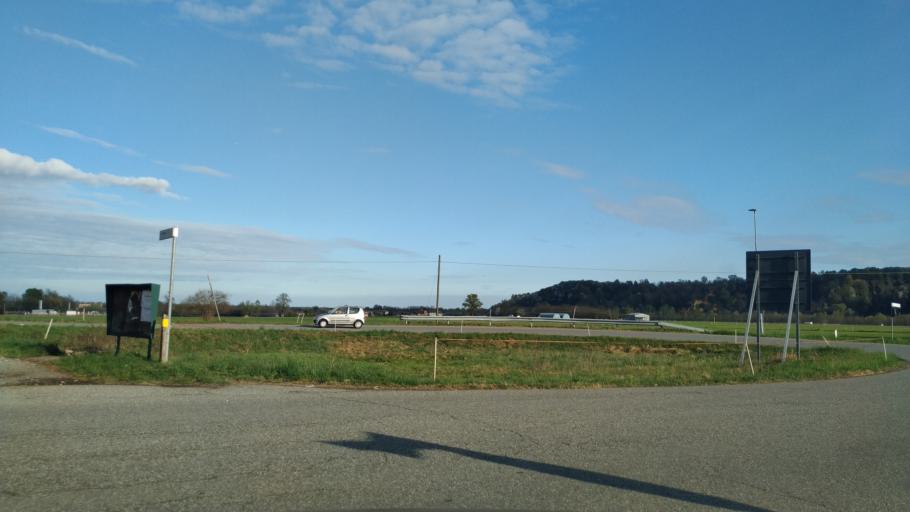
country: IT
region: Piedmont
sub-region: Provincia di Biella
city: Cerreto Castello
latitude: 45.5524
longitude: 8.1572
